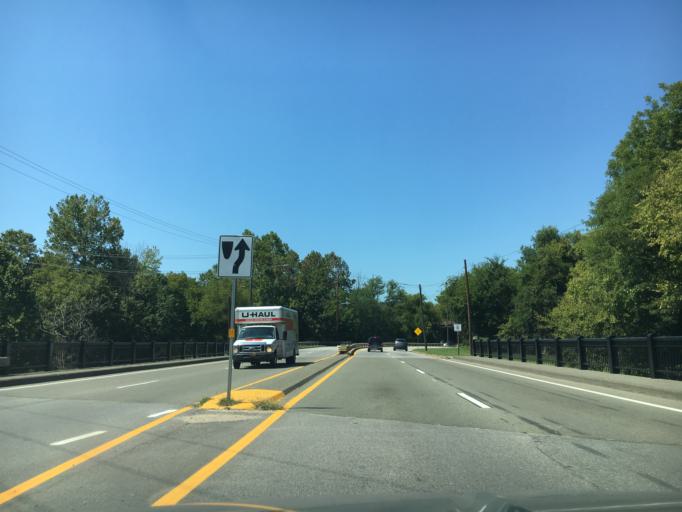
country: US
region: Virginia
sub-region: City of Danville
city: Danville
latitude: 36.5868
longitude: -79.3785
